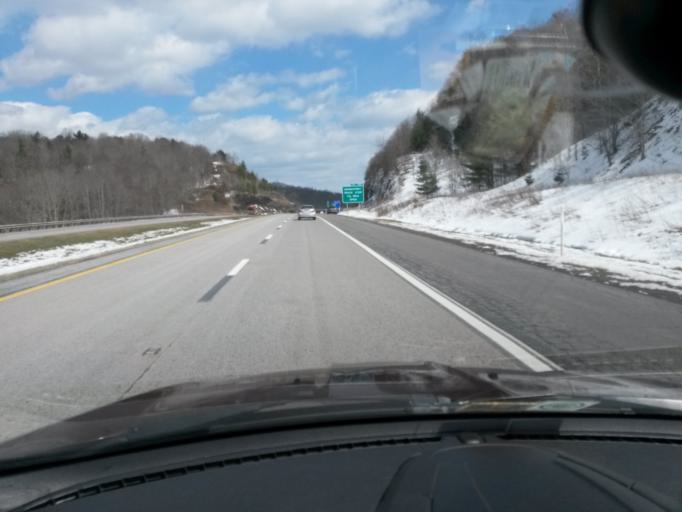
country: US
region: West Virginia
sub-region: Raleigh County
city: Shady Spring
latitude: 37.7674
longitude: -81.0047
